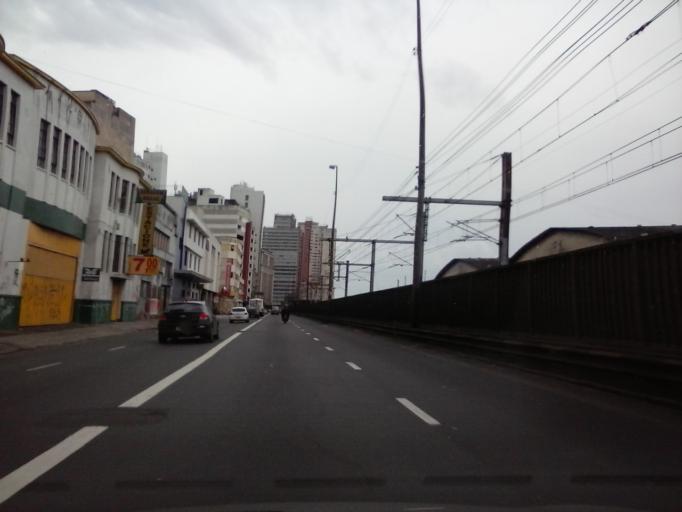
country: BR
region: Rio Grande do Sul
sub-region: Porto Alegre
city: Porto Alegre
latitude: -30.0246
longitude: -51.2239
